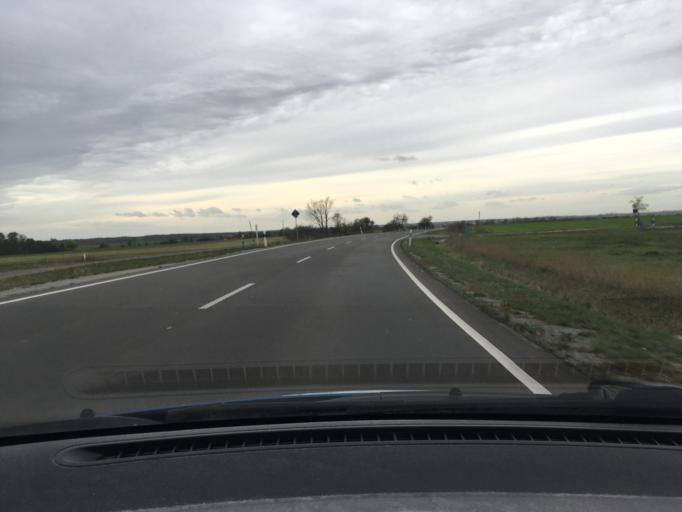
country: DE
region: Saxony-Anhalt
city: Leitzkau
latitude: 52.0599
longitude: 11.9206
